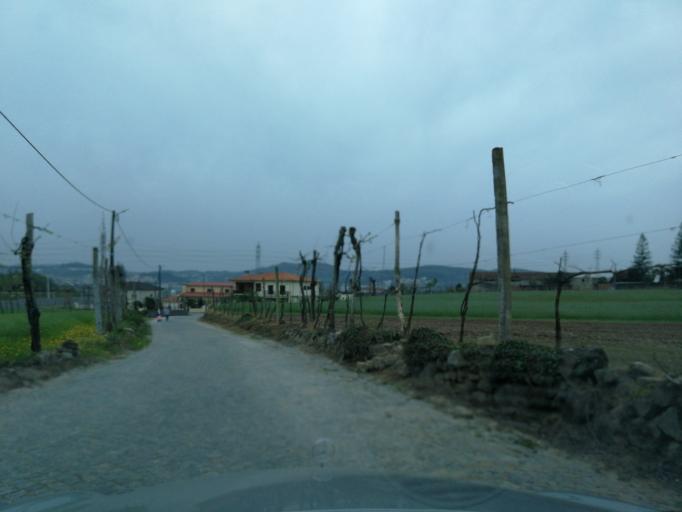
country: PT
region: Braga
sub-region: Braga
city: Braga
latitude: 41.5774
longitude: -8.4397
